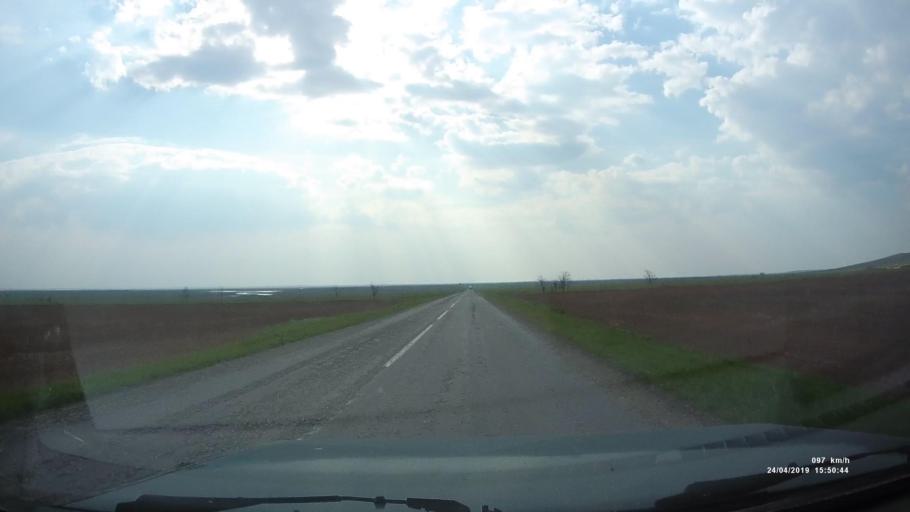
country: RU
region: Kalmykiya
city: Yashalta
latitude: 46.6042
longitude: 42.6265
